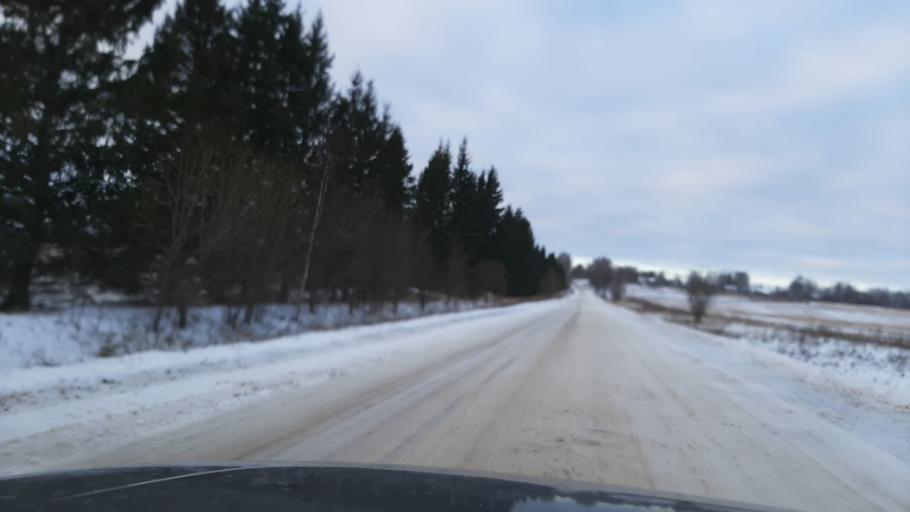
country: RU
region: Kostroma
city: Kosmynino
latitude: 57.4819
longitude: 40.7821
